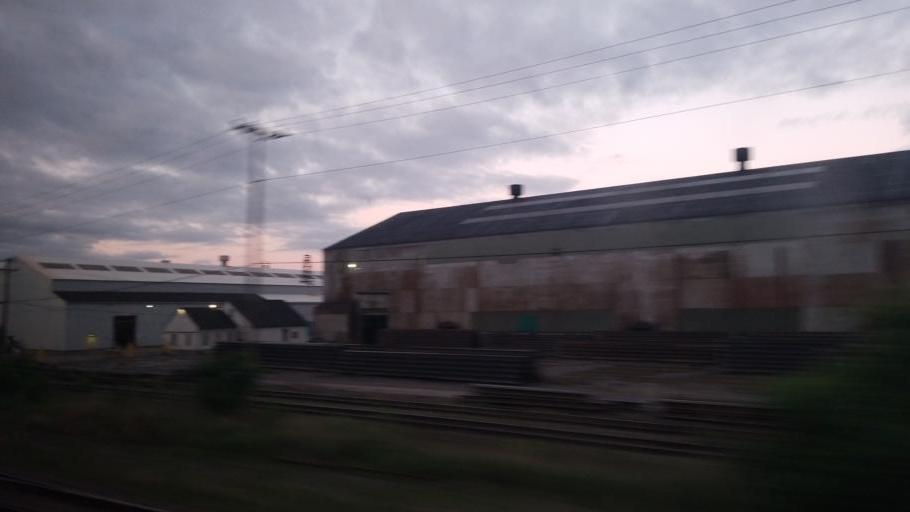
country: US
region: Pennsylvania
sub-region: Beaver County
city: Ambridge
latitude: 40.5848
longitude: -80.2303
